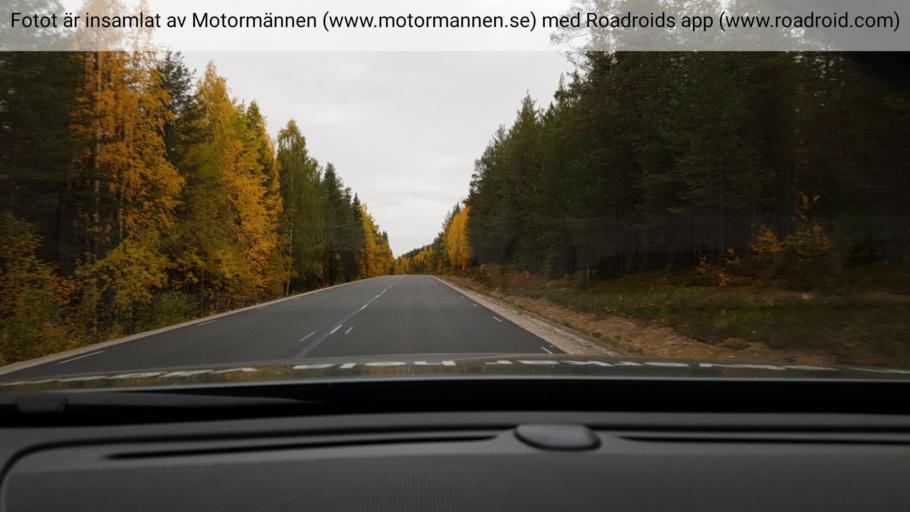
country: SE
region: Norrbotten
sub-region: Overkalix Kommun
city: OEverkalix
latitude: 66.4699
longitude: 22.7921
